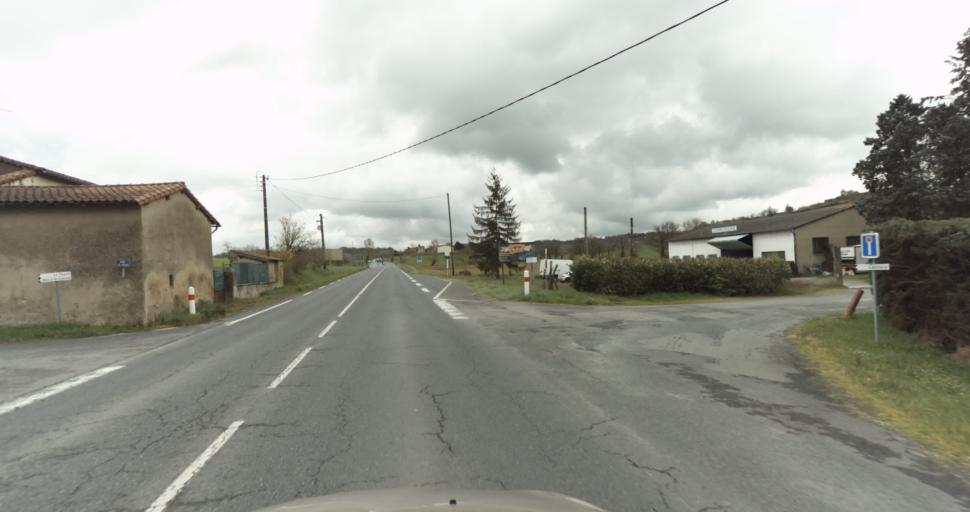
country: FR
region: Midi-Pyrenees
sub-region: Departement du Tarn
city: Puygouzon
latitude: 43.8833
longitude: 2.1690
